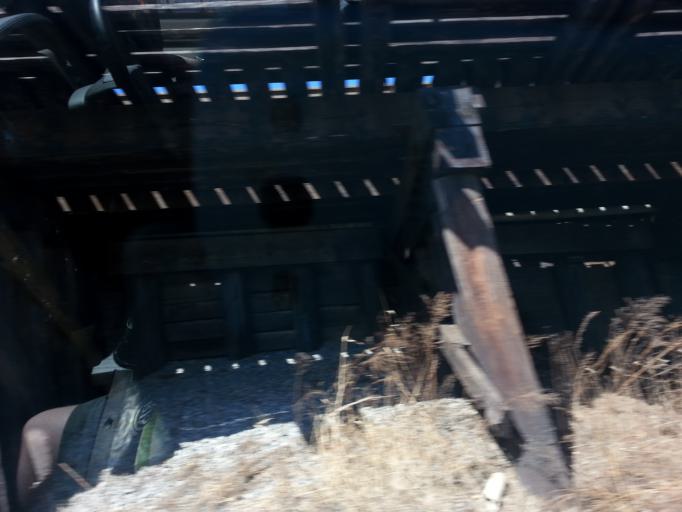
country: US
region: Minnesota
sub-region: Ramsey County
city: Saint Paul
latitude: 44.9443
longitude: -93.0893
